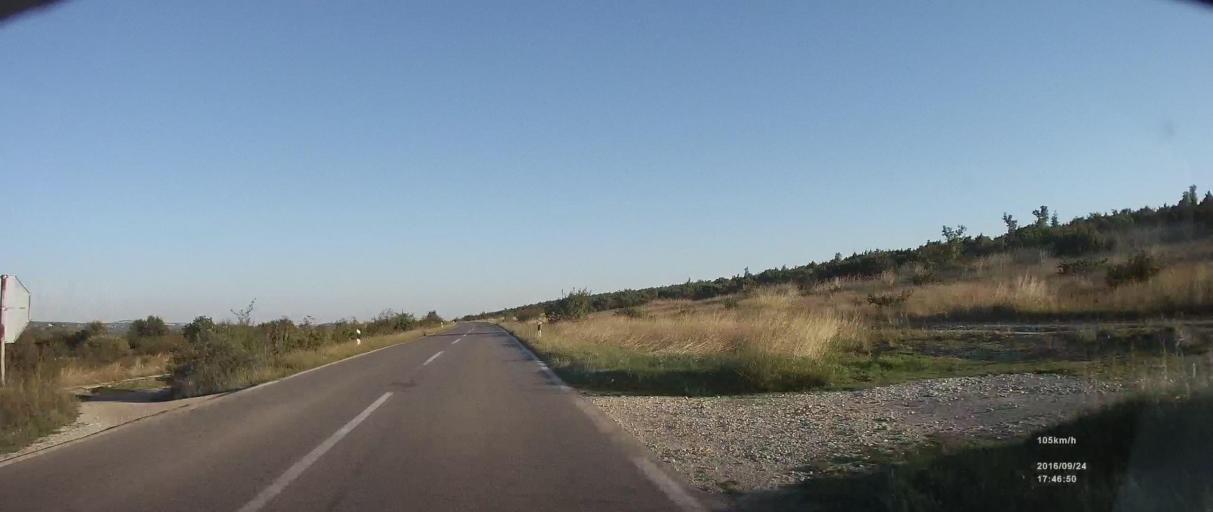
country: HR
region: Zadarska
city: Polaca
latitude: 44.0828
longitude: 15.5136
